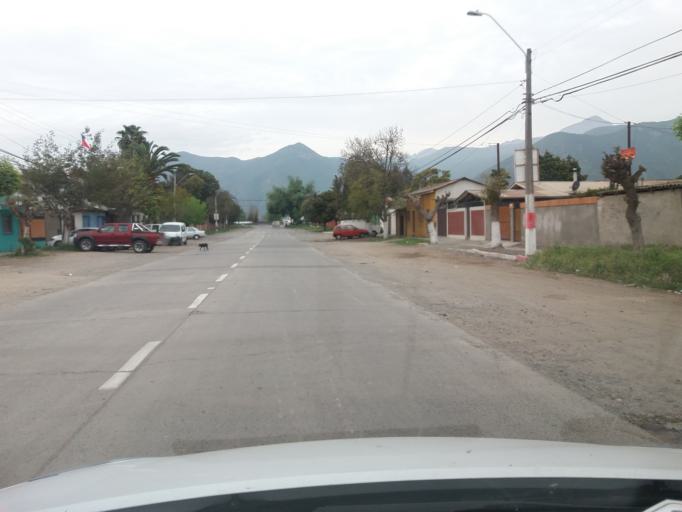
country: CL
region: Valparaiso
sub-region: Provincia de Quillota
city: Hacienda La Calera
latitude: -32.7790
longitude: -71.1826
